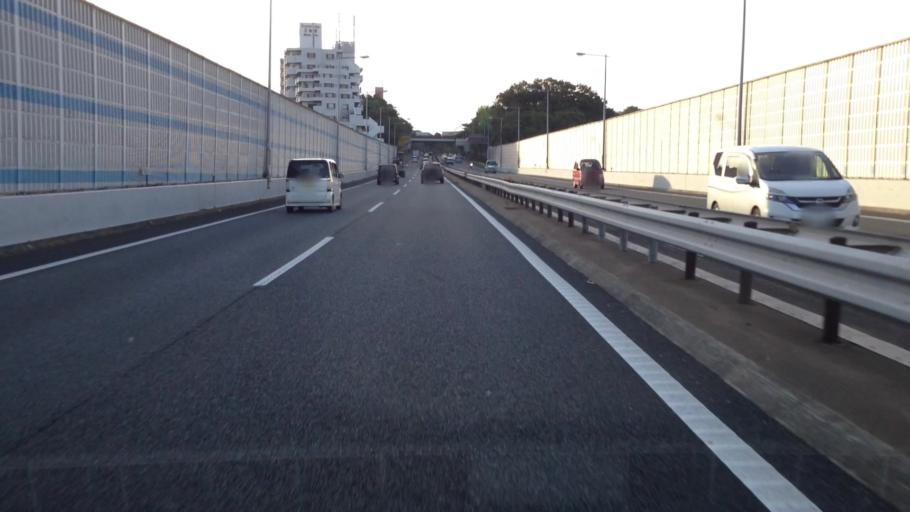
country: JP
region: Kanagawa
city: Kamakura
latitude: 35.3855
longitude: 139.5806
